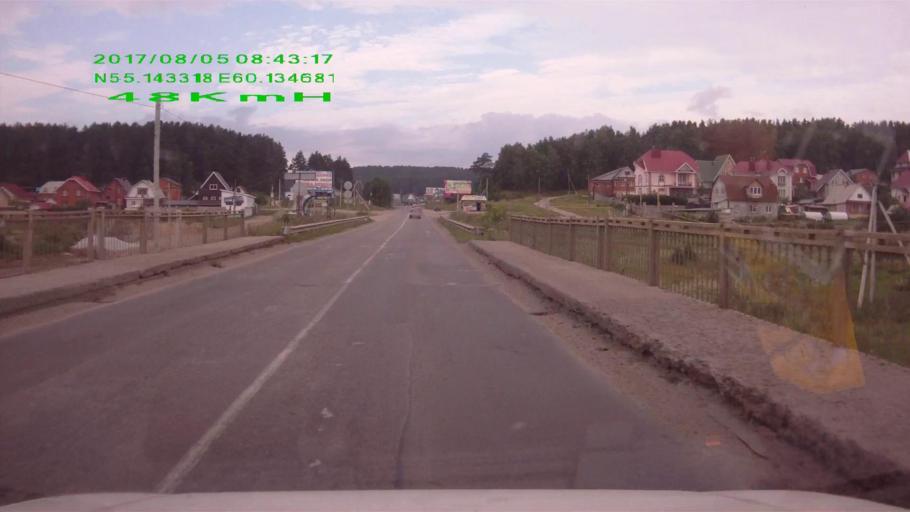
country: RU
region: Chelyabinsk
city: Turgoyak
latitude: 55.1434
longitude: 60.1342
